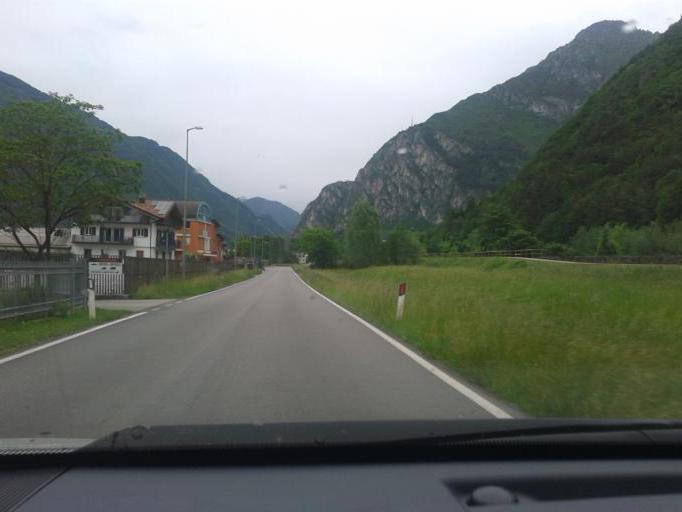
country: IT
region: Trentino-Alto Adige
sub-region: Provincia di Trento
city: Storo
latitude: 45.8383
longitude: 10.5656
